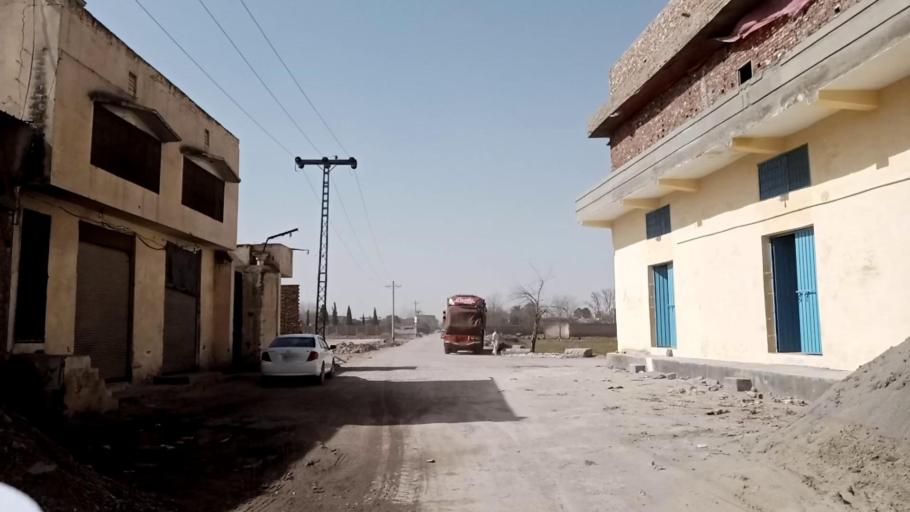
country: PK
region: Khyber Pakhtunkhwa
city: Peshawar
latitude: 34.0169
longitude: 71.6378
